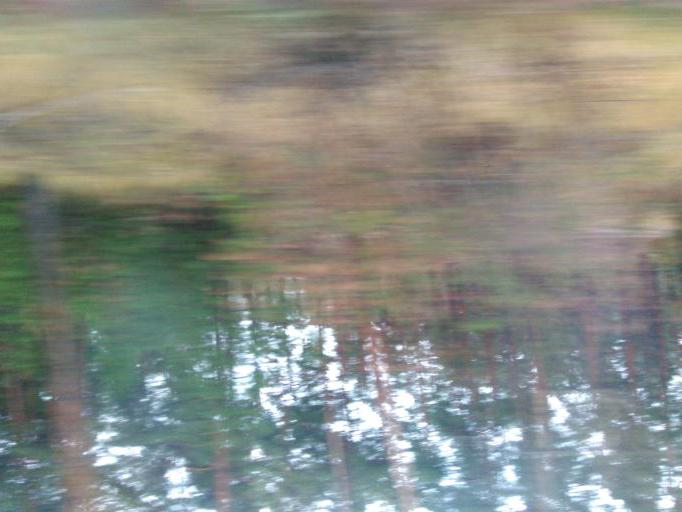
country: RU
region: Tatarstan
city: Osinovo
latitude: 55.8247
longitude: 48.8975
